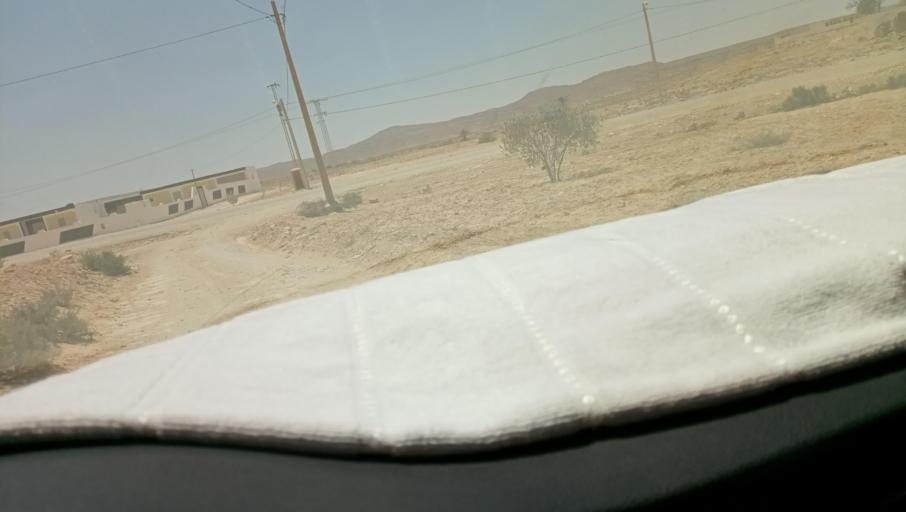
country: TN
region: Tataouine
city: Tataouine
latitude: 32.8527
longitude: 10.5339
